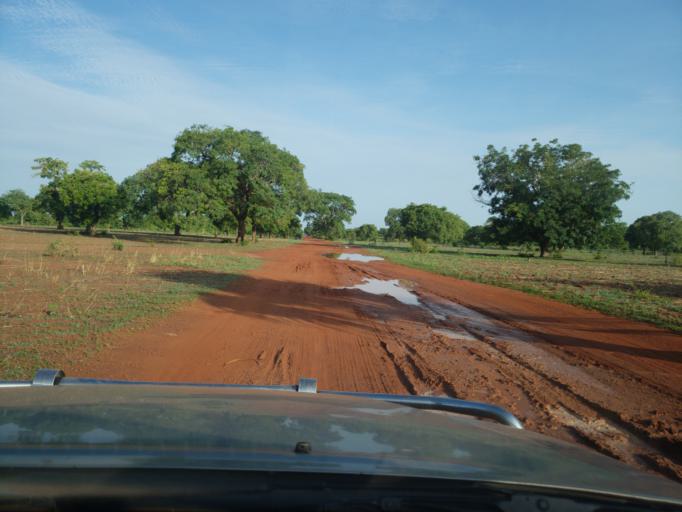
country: ML
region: Sikasso
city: Koutiala
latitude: 12.4254
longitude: -5.5951
